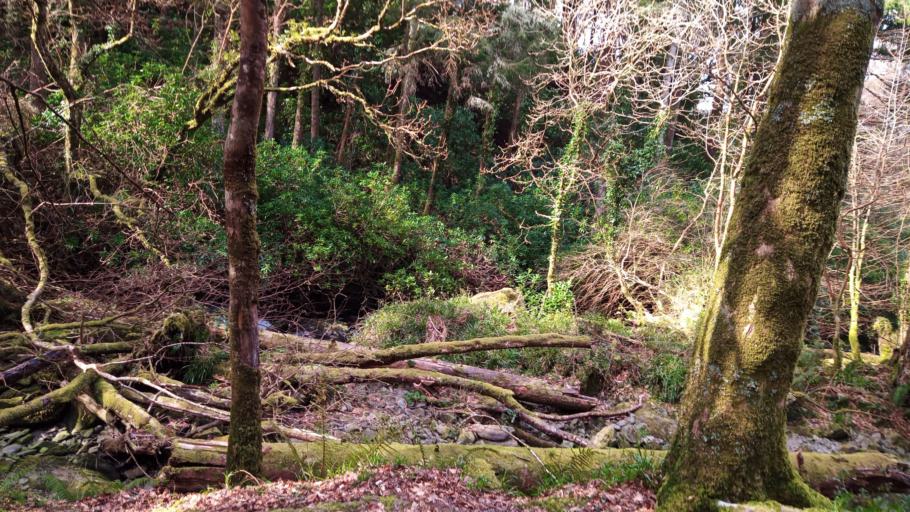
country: IE
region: Munster
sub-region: Ciarrai
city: Cill Airne
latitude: 52.0049
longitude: -9.5063
